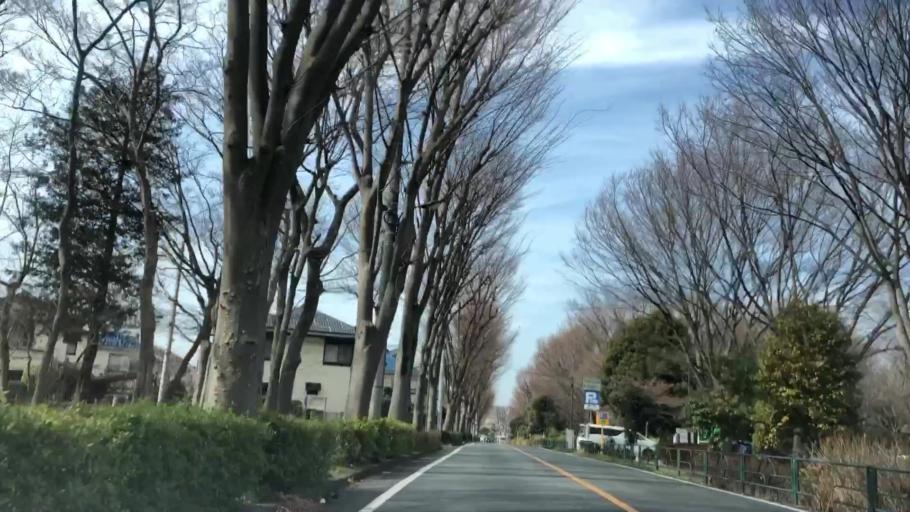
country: JP
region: Saitama
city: Wako
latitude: 35.7742
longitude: 139.5977
